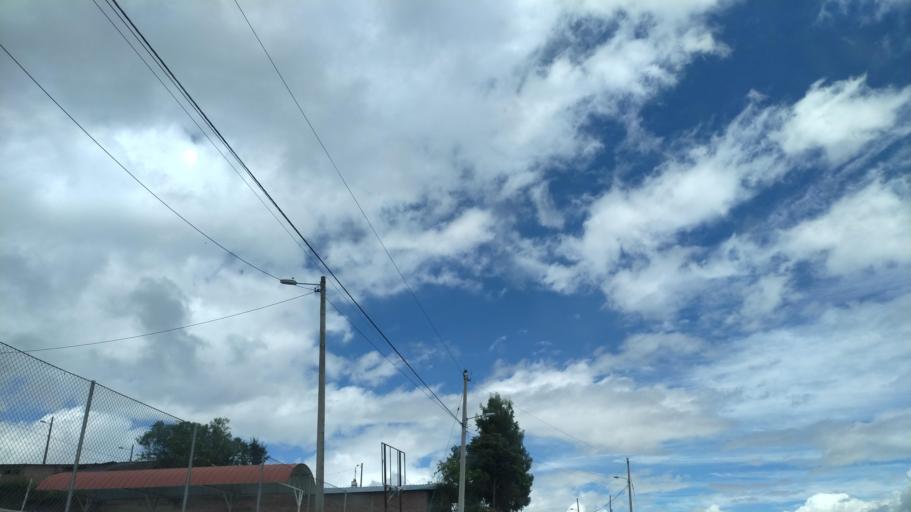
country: EC
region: Chimborazo
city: Riobamba
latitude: -1.6793
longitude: -78.5742
